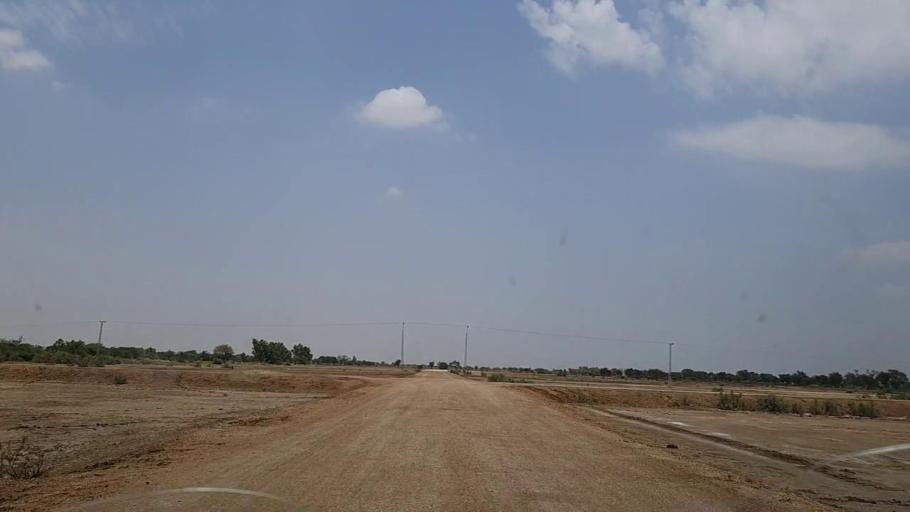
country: PK
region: Sindh
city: Phulji
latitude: 26.8166
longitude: 67.6340
